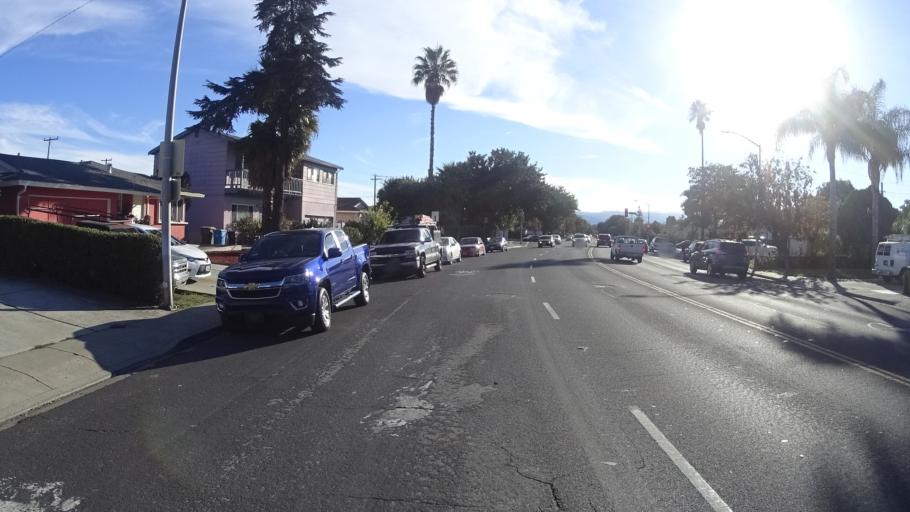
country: US
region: California
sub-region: Santa Clara County
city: Santa Clara
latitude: 37.3614
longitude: -121.9756
